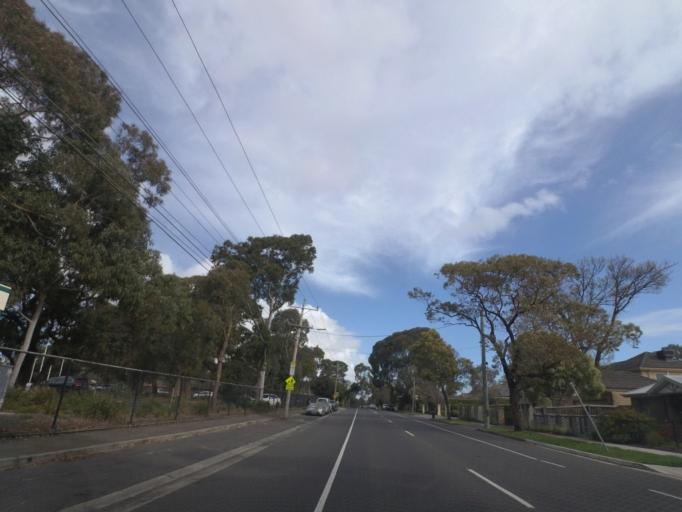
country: AU
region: Victoria
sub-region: Whitehorse
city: Vermont
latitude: -37.8376
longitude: 145.1910
